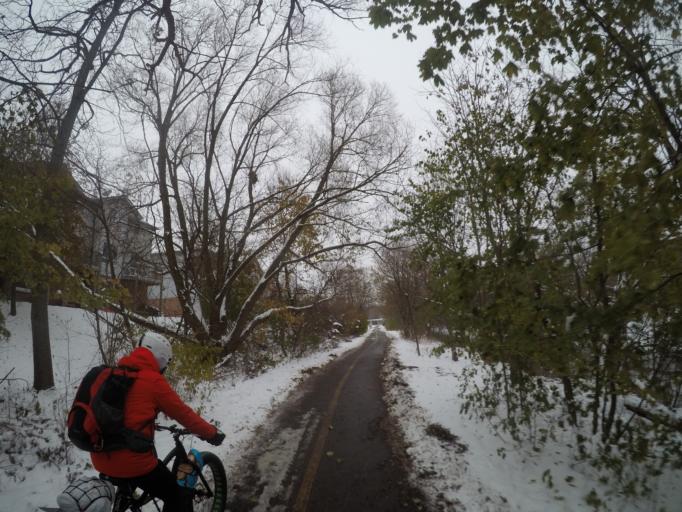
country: CA
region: Ontario
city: Waterloo
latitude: 43.4710
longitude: -80.5163
